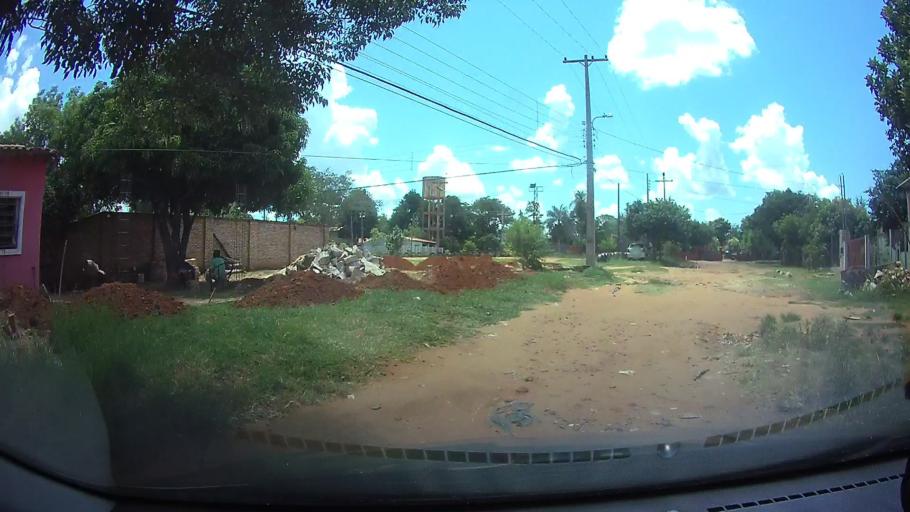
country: PY
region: Central
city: Limpio
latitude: -25.1532
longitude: -57.4555
